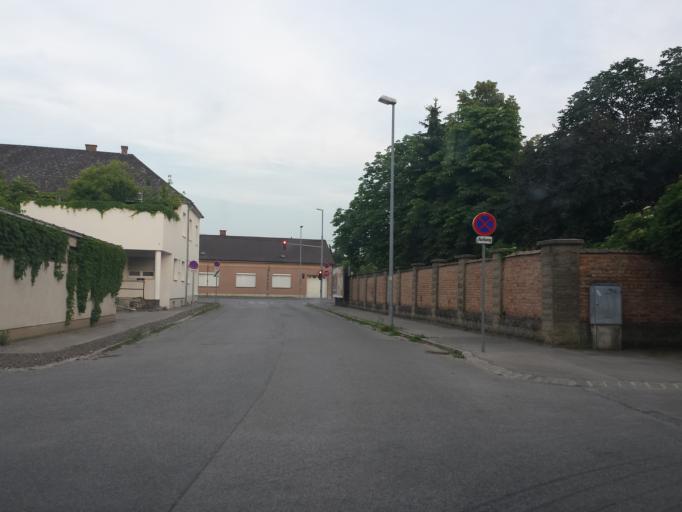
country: AT
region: Lower Austria
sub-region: Politischer Bezirk Ganserndorf
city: Deutsch-Wagram
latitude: 48.2975
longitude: 16.5603
